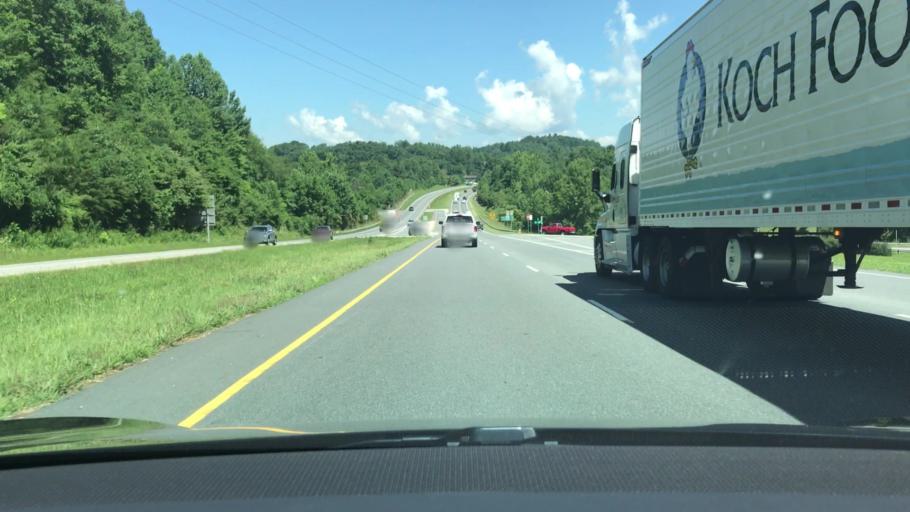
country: US
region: North Carolina
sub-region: Macon County
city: Franklin
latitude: 35.1869
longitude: -83.3589
